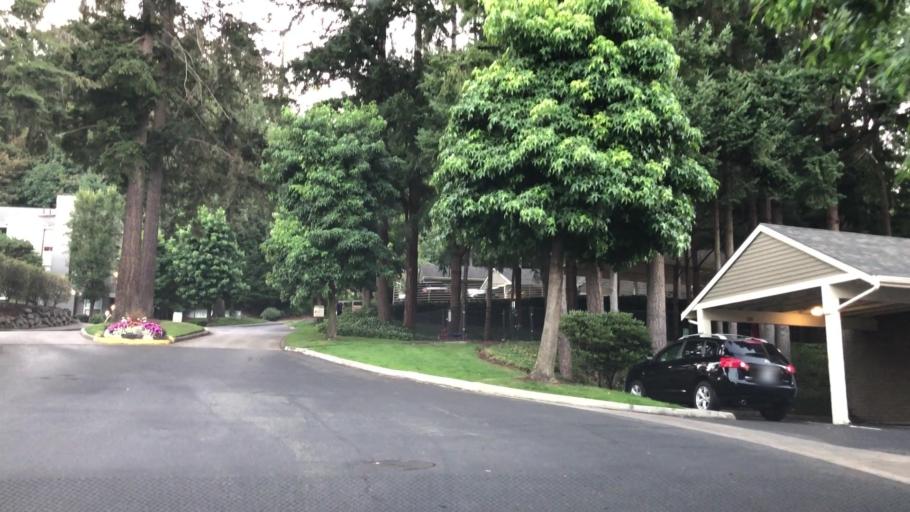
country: US
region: Washington
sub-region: King County
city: Redmond
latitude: 47.6822
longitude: -122.1034
